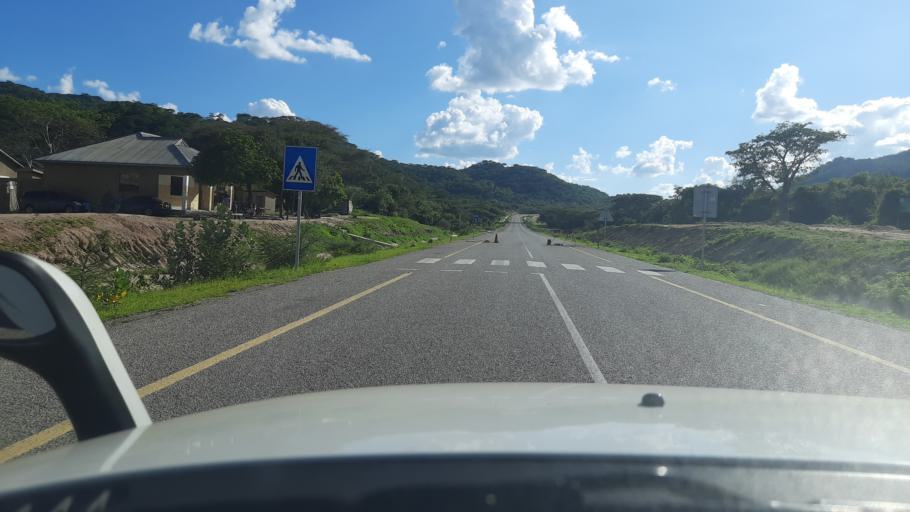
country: TZ
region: Dodoma
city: Msanga
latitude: -5.6246
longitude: 35.8325
